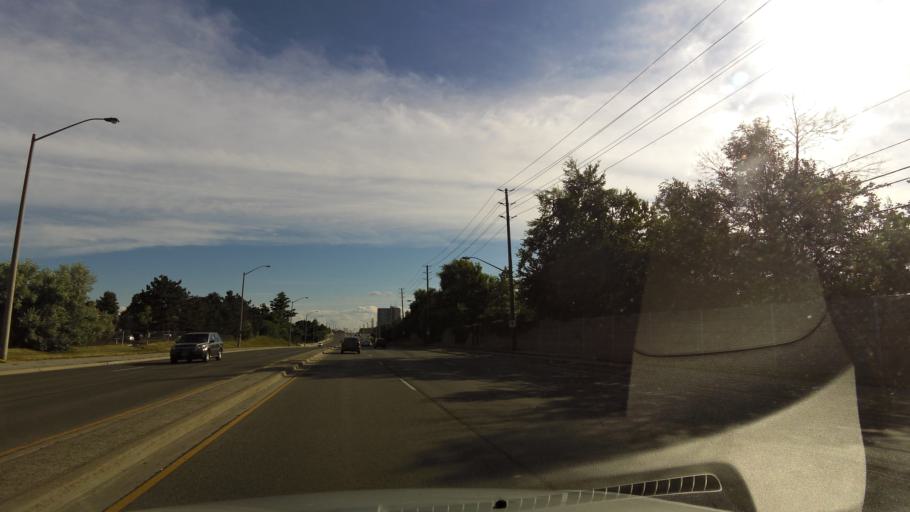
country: CA
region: Ontario
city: Brampton
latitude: 43.6702
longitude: -79.7287
